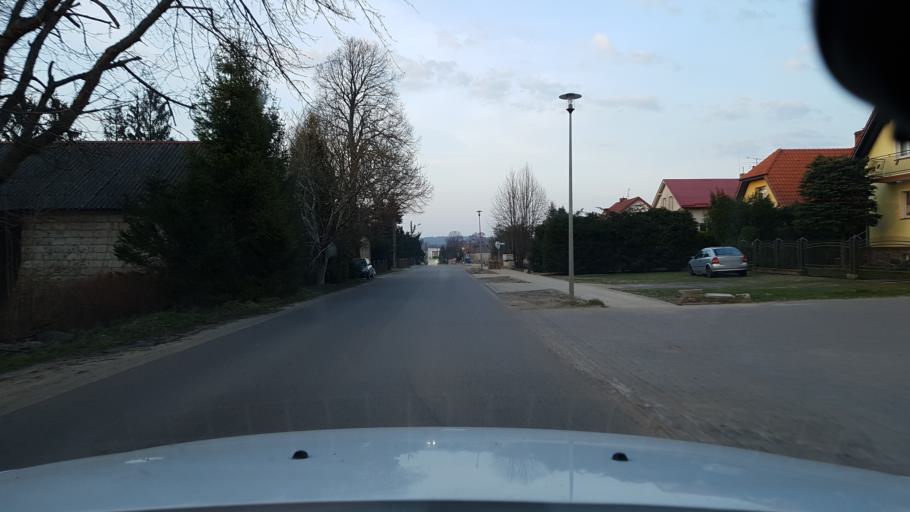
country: PL
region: West Pomeranian Voivodeship
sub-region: Koszalin
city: Koszalin
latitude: 54.1571
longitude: 16.2125
